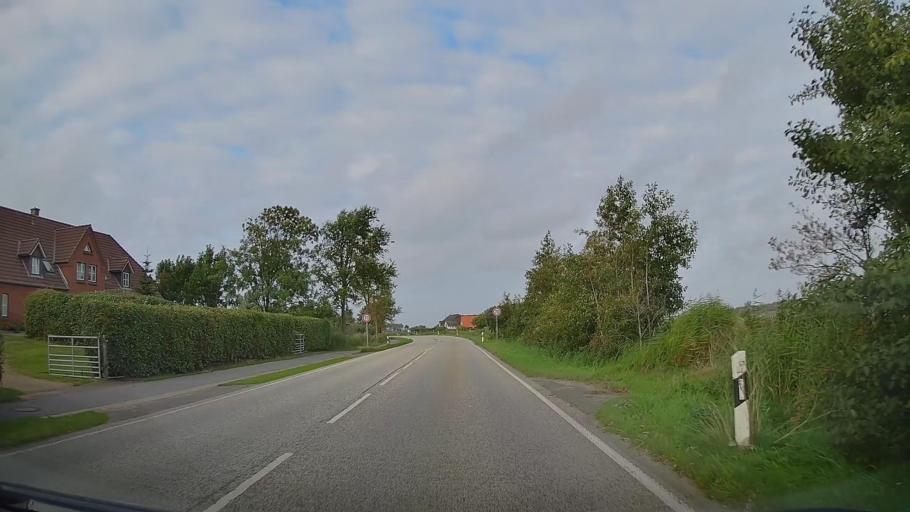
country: DE
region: Schleswig-Holstein
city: Sankt Peter-Ording
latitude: 54.3244
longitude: 8.6123
